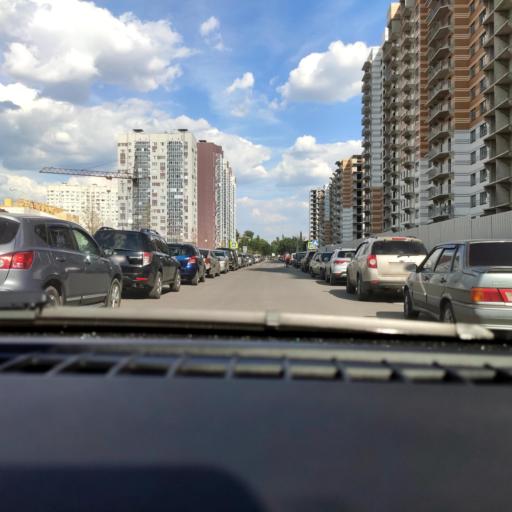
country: RU
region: Voronezj
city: Voronezh
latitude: 51.7136
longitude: 39.2644
